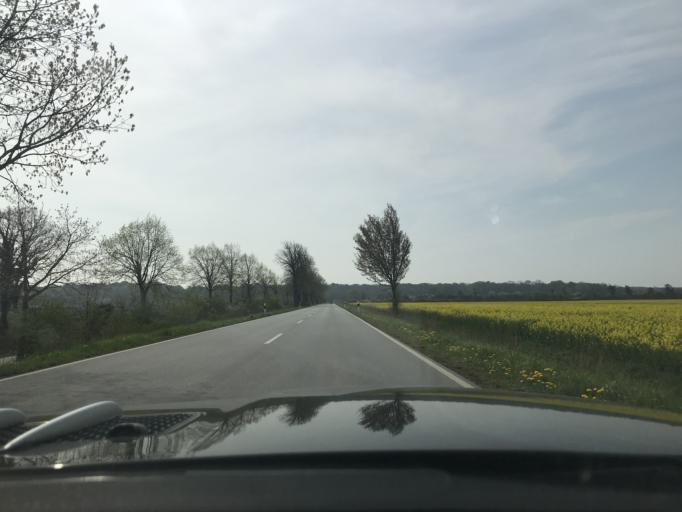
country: DE
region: Schleswig-Holstein
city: Grube
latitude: 54.2138
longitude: 11.0361
